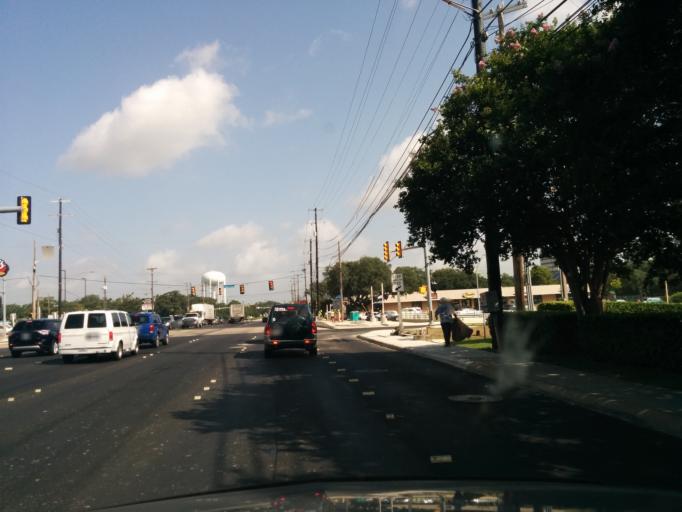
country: US
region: Texas
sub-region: Bexar County
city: Balcones Heights
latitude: 29.5125
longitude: -98.5686
